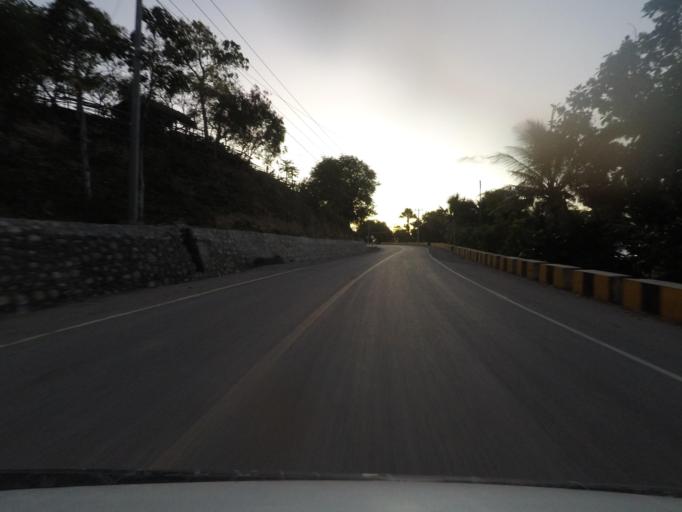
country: TL
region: Baucau
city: Baucau
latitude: -8.4776
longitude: 126.5936
